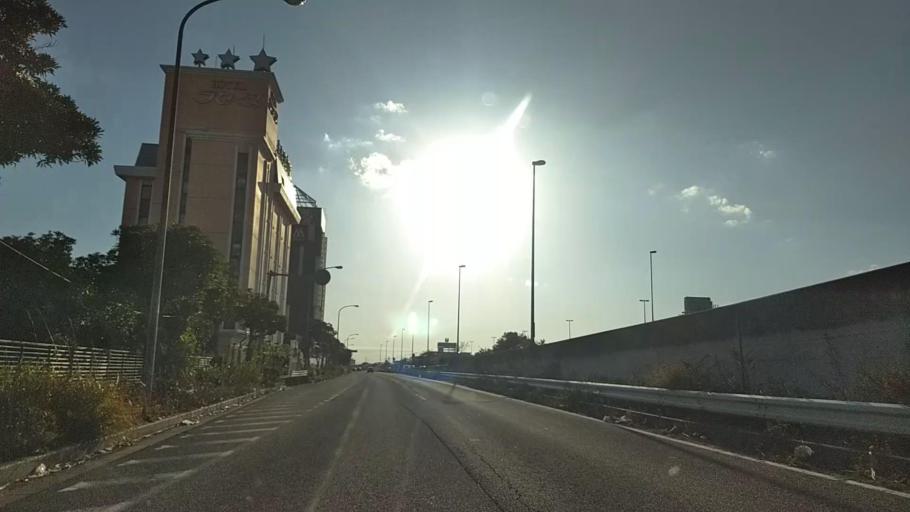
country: JP
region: Tokyo
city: Urayasu
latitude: 35.6697
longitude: 139.9249
